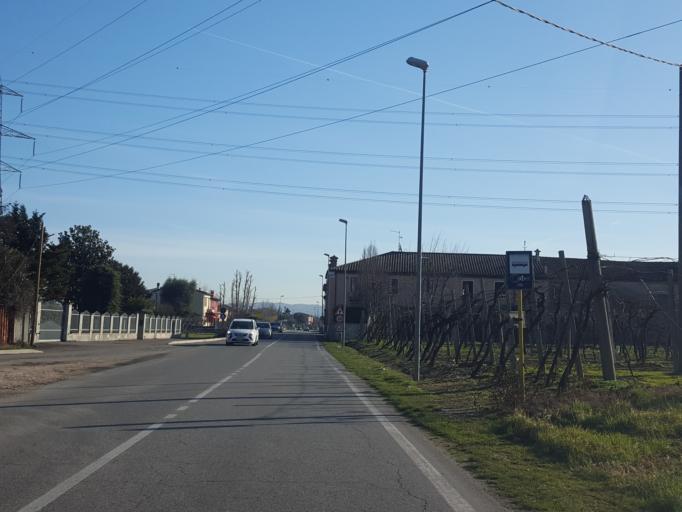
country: IT
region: Veneto
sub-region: Provincia di Verona
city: Locara
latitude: 45.3991
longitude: 11.3197
